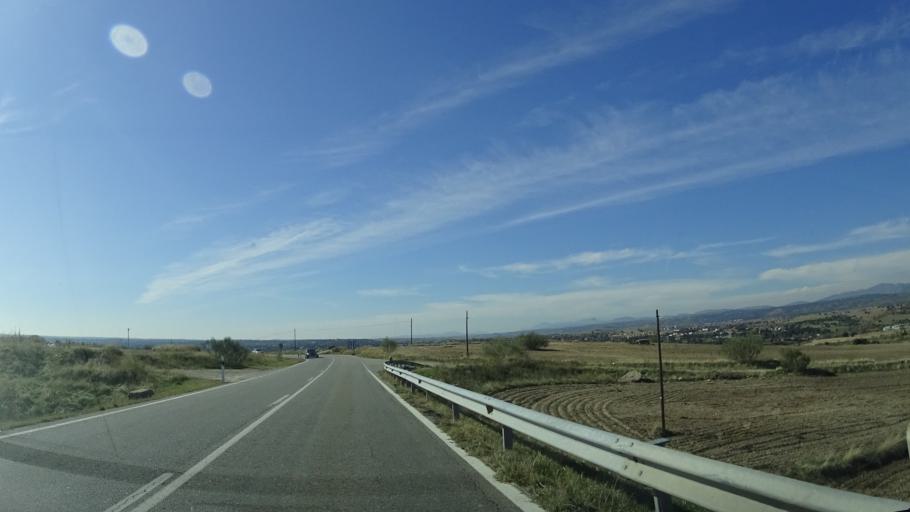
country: ES
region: Madrid
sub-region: Provincia de Madrid
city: Las Rozas de Madrid
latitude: 40.4908
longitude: -3.9187
